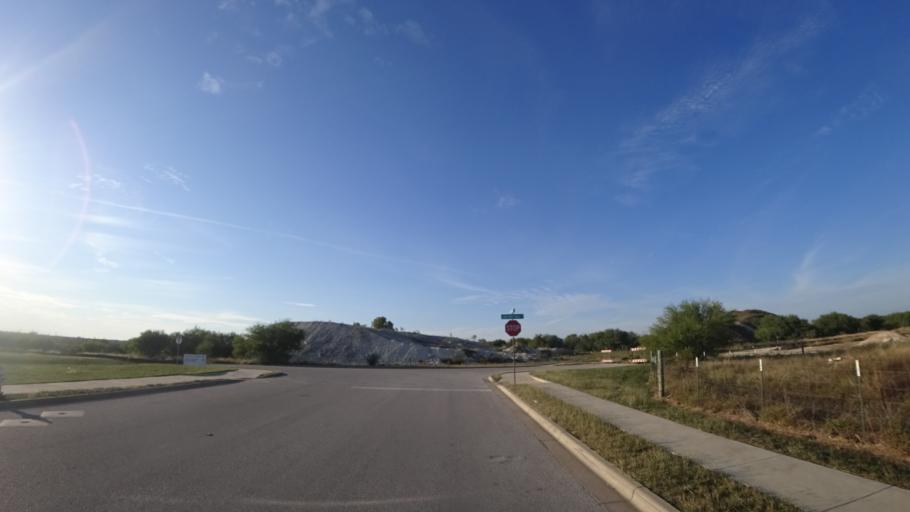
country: US
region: Texas
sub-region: Travis County
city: Pflugerville
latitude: 30.4245
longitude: -97.6477
